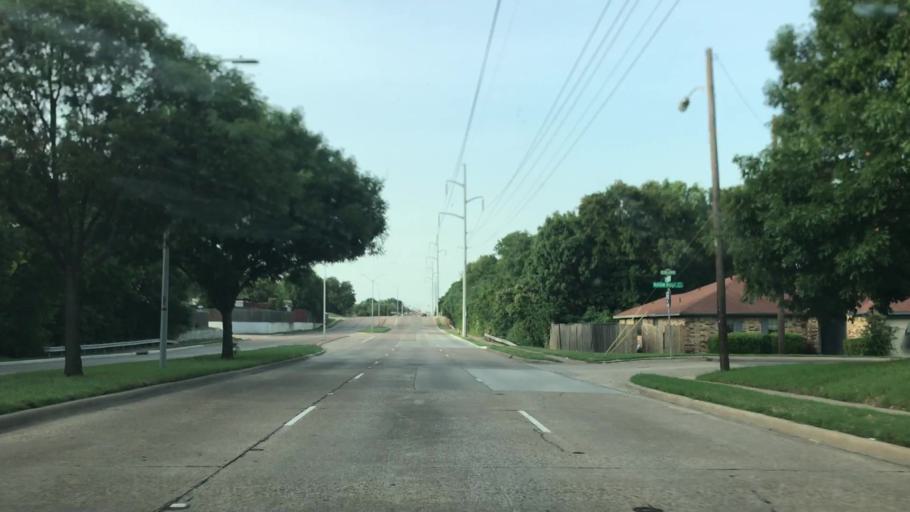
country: US
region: Texas
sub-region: Dallas County
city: Balch Springs
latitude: 32.7824
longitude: -96.7002
